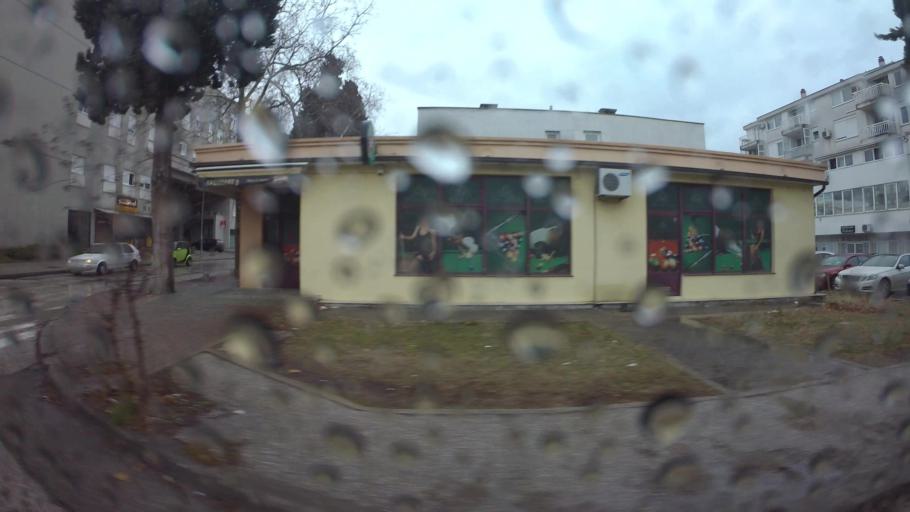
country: BA
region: Federation of Bosnia and Herzegovina
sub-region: Hercegovacko-Bosanski Kanton
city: Mostar
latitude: 43.3520
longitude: 17.7995
